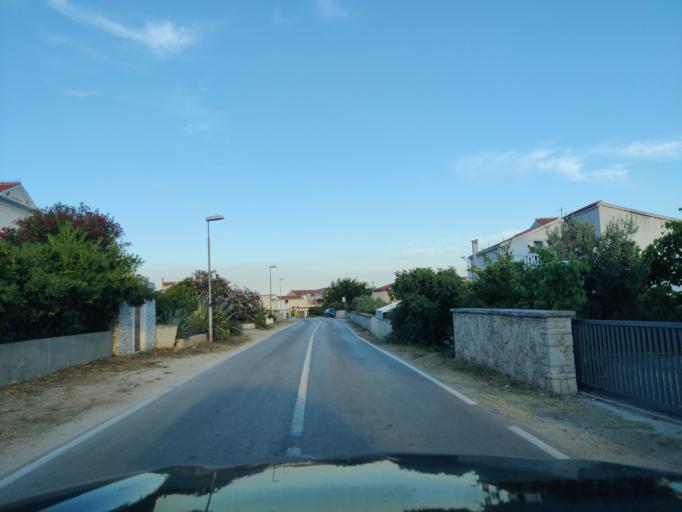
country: HR
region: Sibensko-Kniniska
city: Tribunj
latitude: 43.7605
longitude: 15.7458
